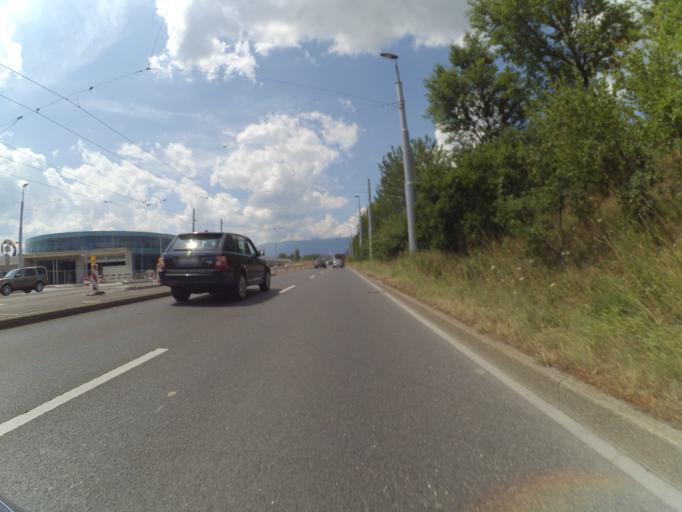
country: CH
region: Geneva
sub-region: Geneva
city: Vernier
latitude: 46.2236
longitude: 6.0917
